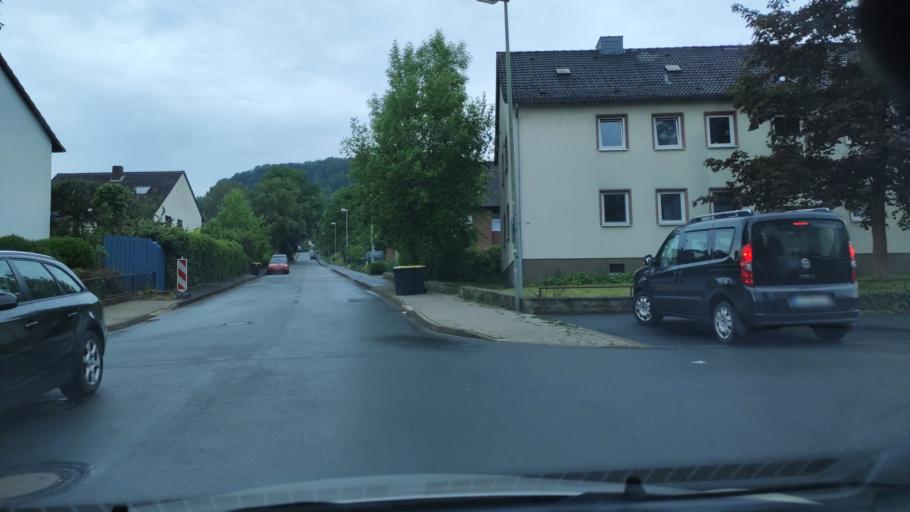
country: DE
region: North Rhine-Westphalia
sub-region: Regierungsbezirk Detmold
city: Hoexter
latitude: 51.7682
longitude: 9.3723
